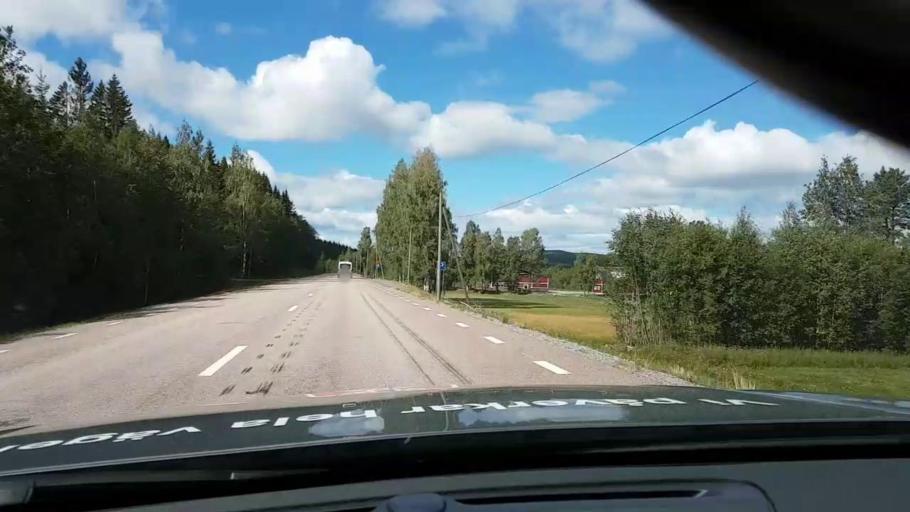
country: SE
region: Vaesternorrland
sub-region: OErnskoeldsviks Kommun
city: Bjasta
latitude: 63.3576
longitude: 18.4792
